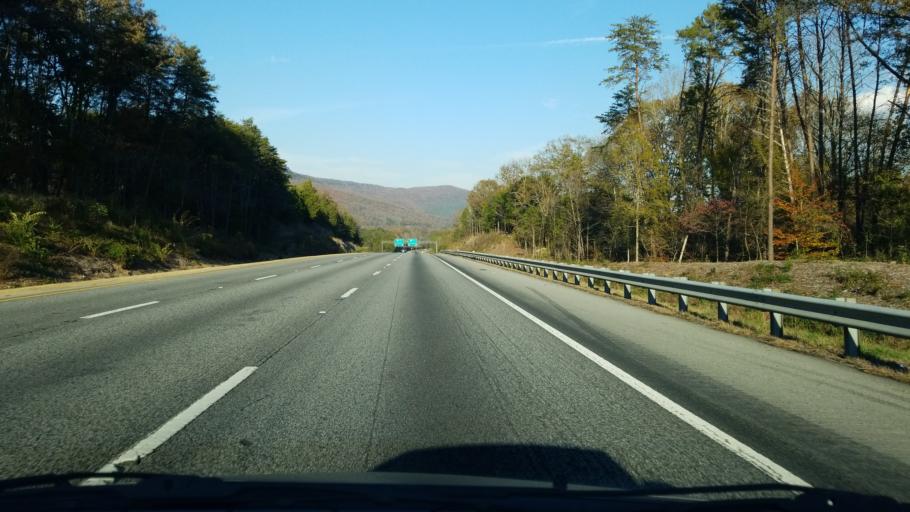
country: US
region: Georgia
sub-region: Walker County
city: Lookout Mountain
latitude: 34.9628
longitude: -85.4557
